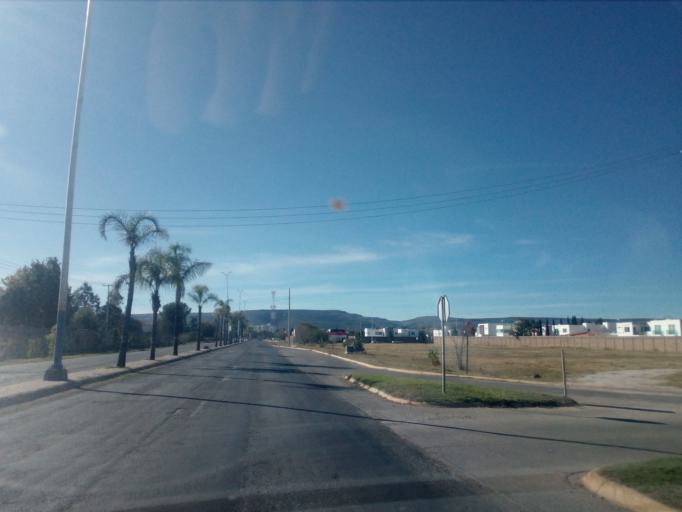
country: MX
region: Durango
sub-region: Durango
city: Sebastian Lerdo de Tejada
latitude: 23.9750
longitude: -104.6648
